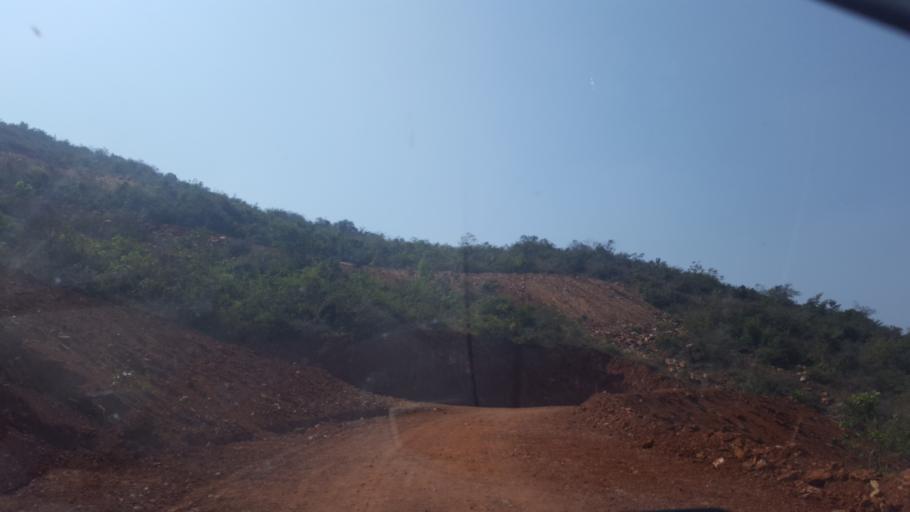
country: IN
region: Andhra Pradesh
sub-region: Srikakulam
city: Palasa
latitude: 18.7208
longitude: 84.3951
